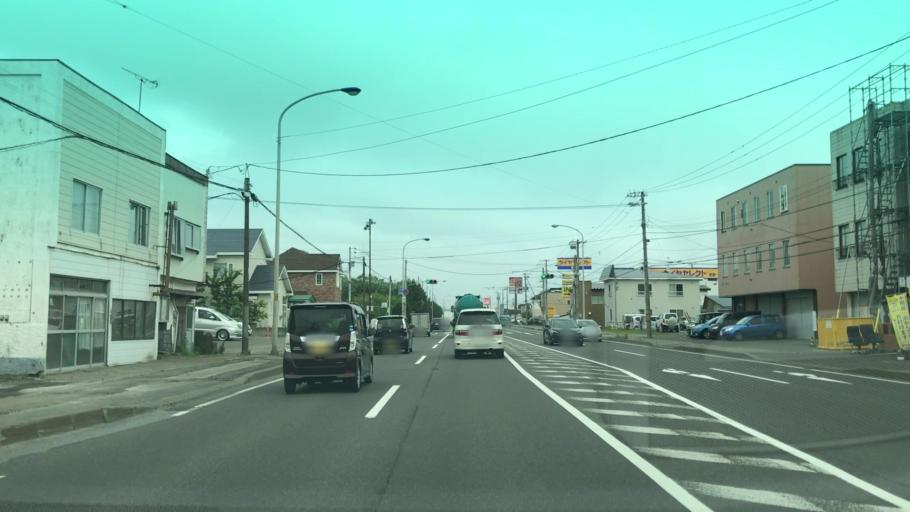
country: JP
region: Hokkaido
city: Muroran
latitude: 42.3588
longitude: 141.0521
